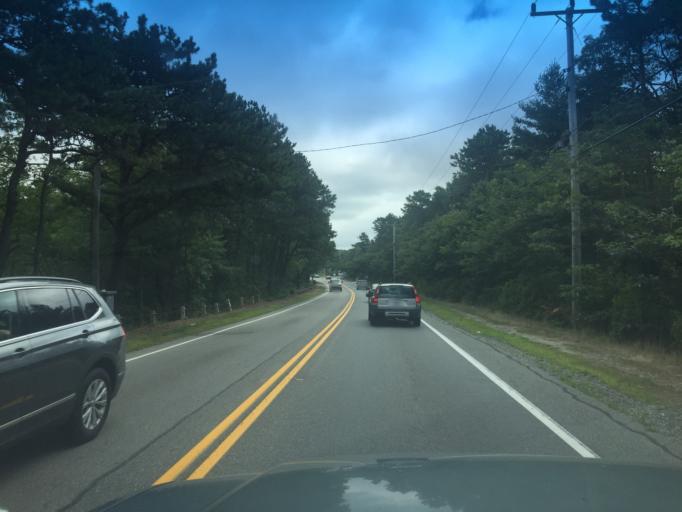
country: US
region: Massachusetts
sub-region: Barnstable County
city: East Falmouth
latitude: 41.6157
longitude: -70.5231
